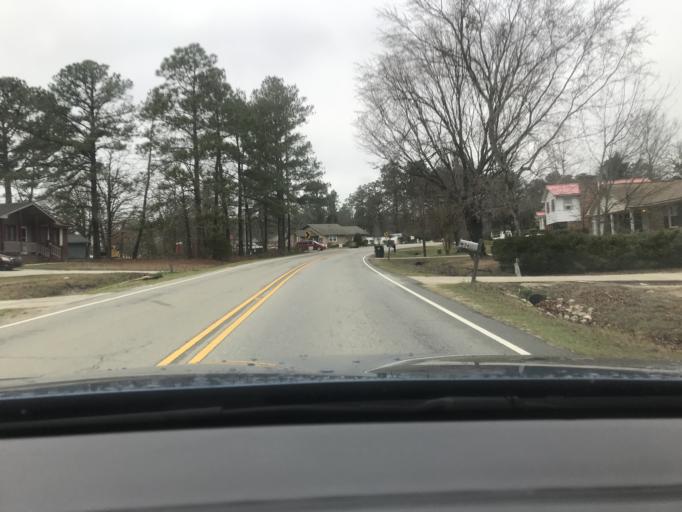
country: US
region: North Carolina
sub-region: Hoke County
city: Rockfish
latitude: 35.0239
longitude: -79.0109
